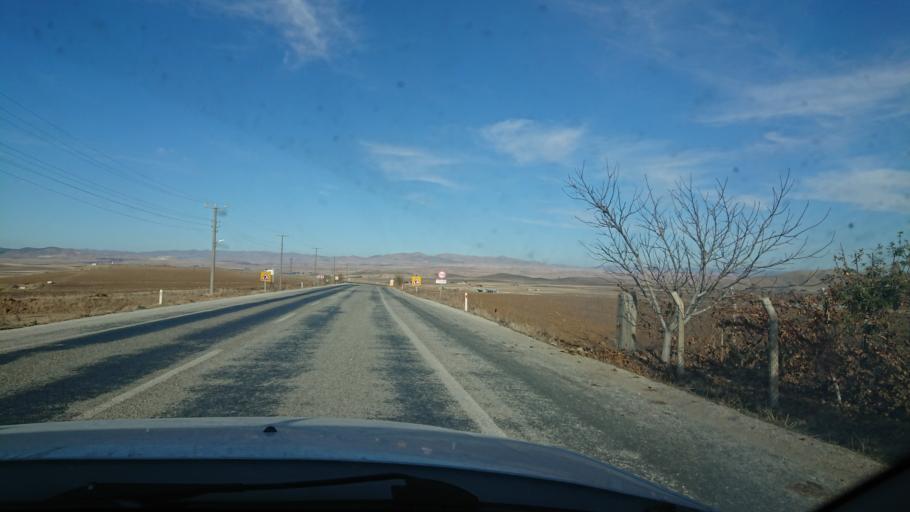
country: TR
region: Aksaray
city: Sariyahsi
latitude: 38.9948
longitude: 33.8495
